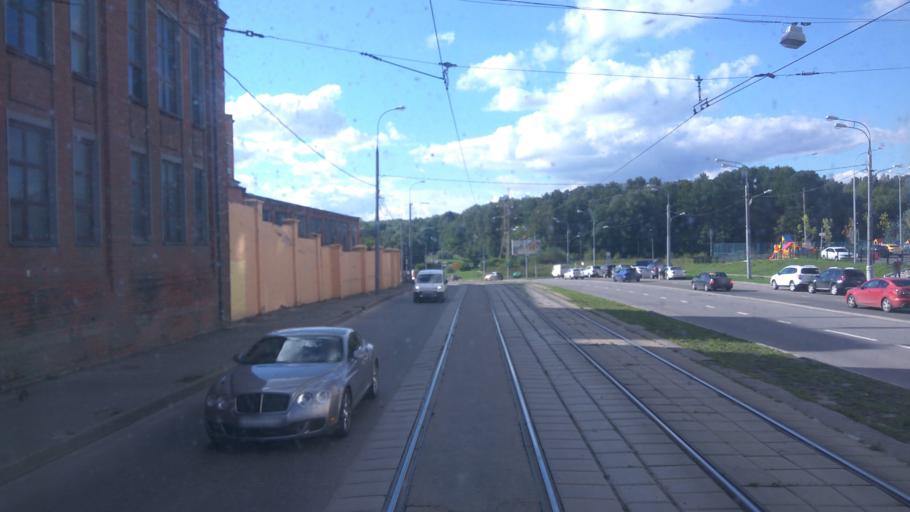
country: RU
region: Moskovskaya
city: Bogorodskoye
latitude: 55.8159
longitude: 37.6918
